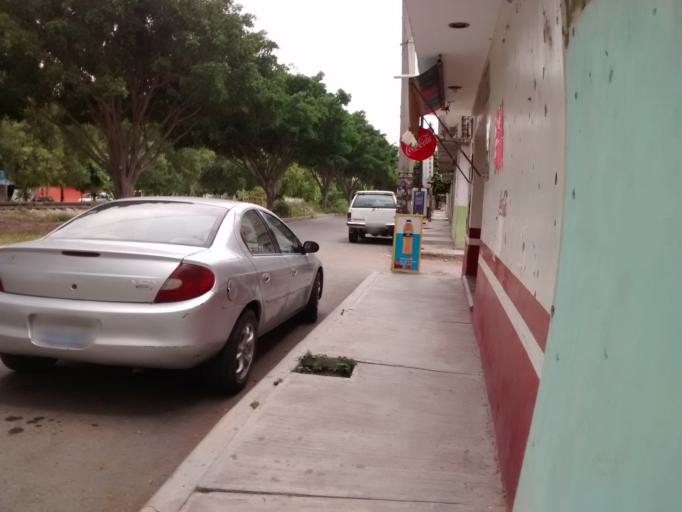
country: MX
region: Puebla
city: Tehuacan
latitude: 18.4716
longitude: -97.4061
